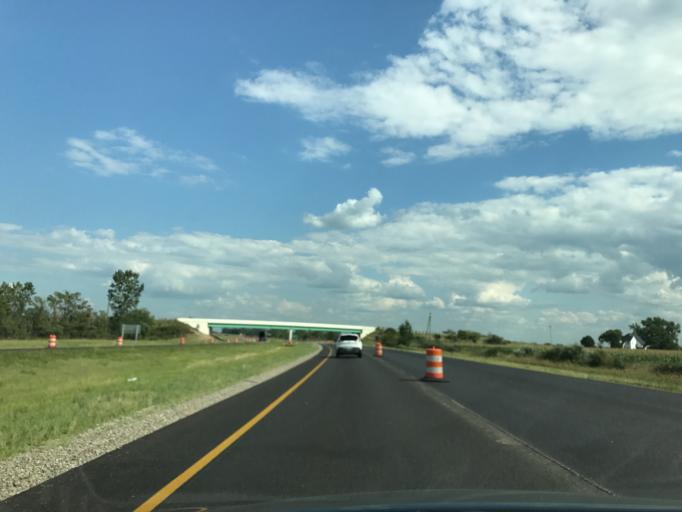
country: US
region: Ohio
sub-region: Van Wert County
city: Van Wert
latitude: 40.8726
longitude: -84.5169
